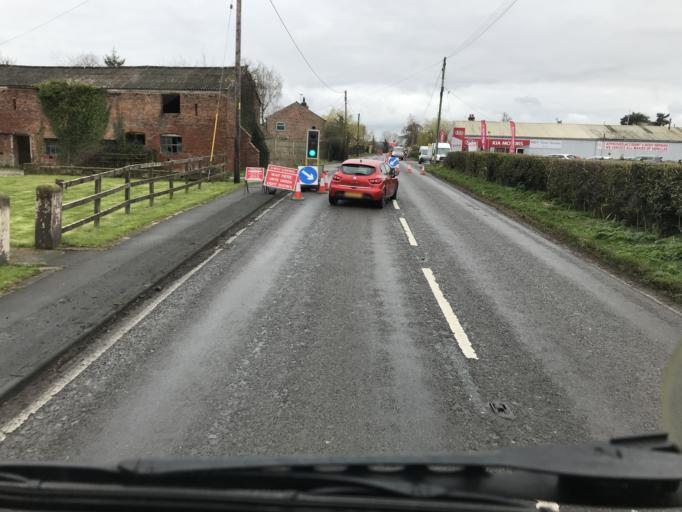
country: GB
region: England
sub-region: Cheshire West and Chester
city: Tattenhall
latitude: 53.1249
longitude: -2.8062
